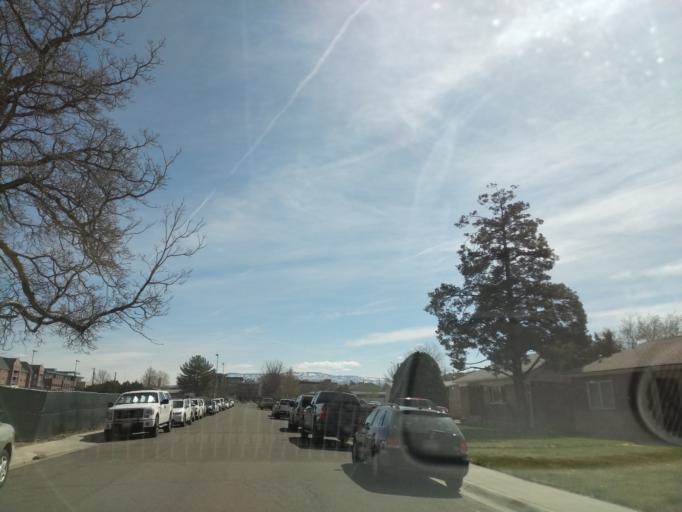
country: US
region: Colorado
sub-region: Mesa County
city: Grand Junction
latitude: 39.0802
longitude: -108.5596
